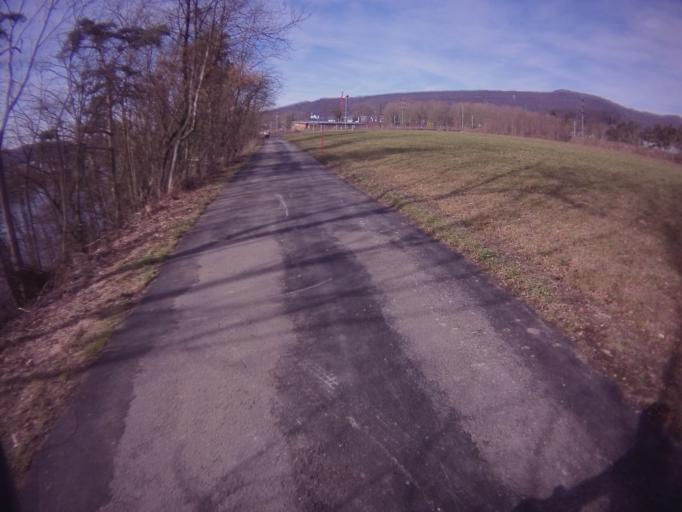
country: CH
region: Aargau
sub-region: Bezirk Baden
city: Neuenhof
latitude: 47.4523
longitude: 8.3348
